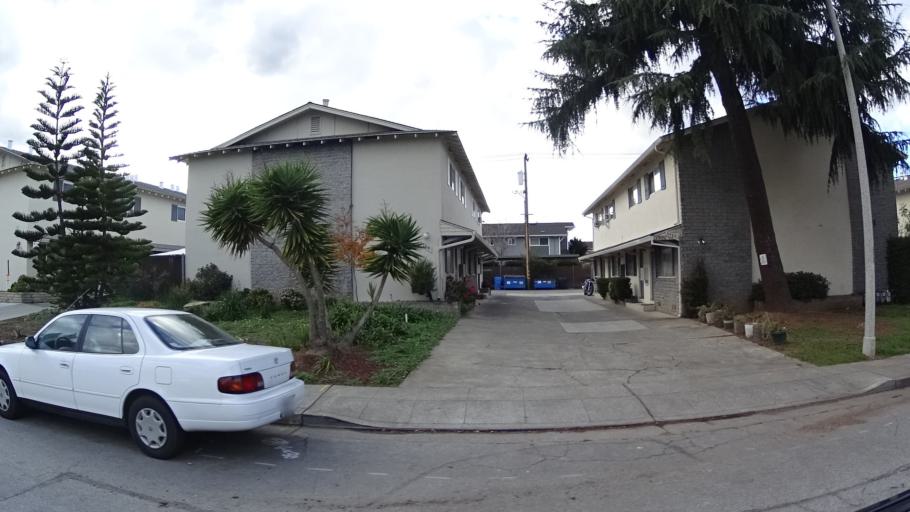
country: US
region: California
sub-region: Santa Clara County
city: Cupertino
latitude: 37.3363
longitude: -122.0443
